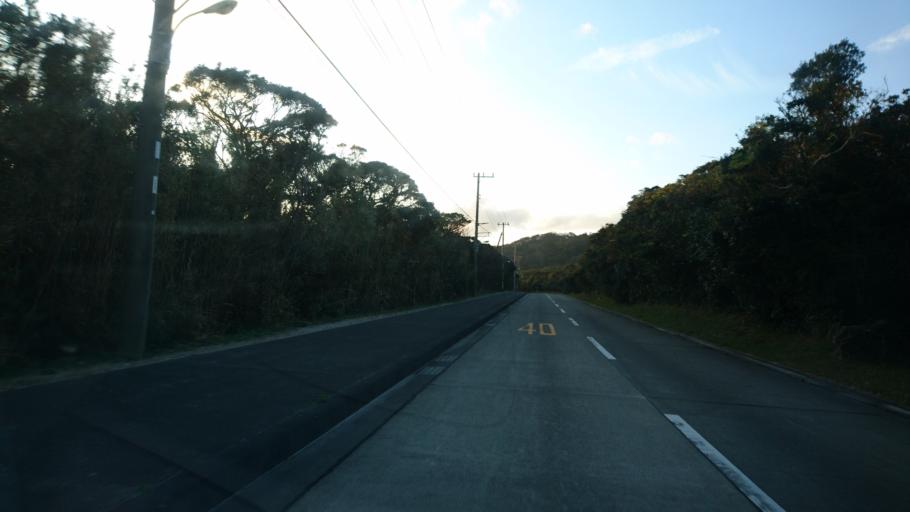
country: JP
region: Shizuoka
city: Shimoda
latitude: 34.3631
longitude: 139.2542
